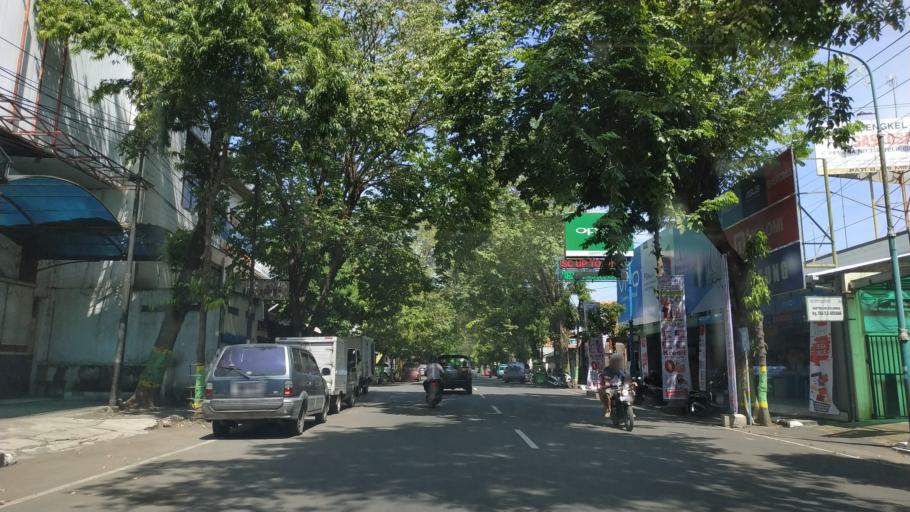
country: ID
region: Central Java
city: Baran
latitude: -6.7531
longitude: 111.0503
